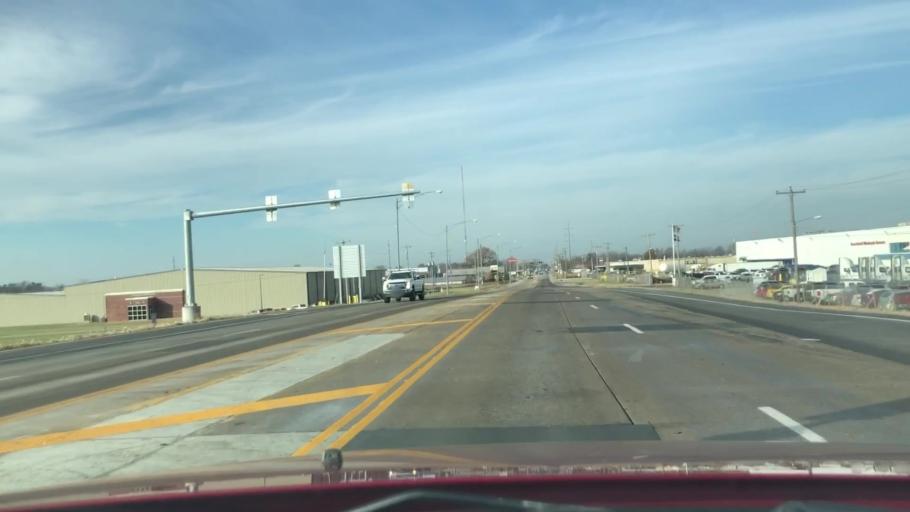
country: US
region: Missouri
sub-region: Greene County
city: Springfield
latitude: 37.2243
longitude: -93.2263
